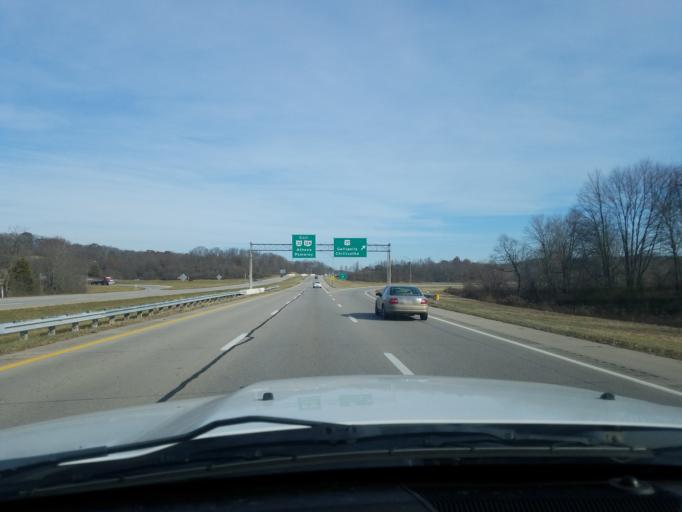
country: US
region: Ohio
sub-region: Jackson County
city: Jackson
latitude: 39.0430
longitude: -82.6178
